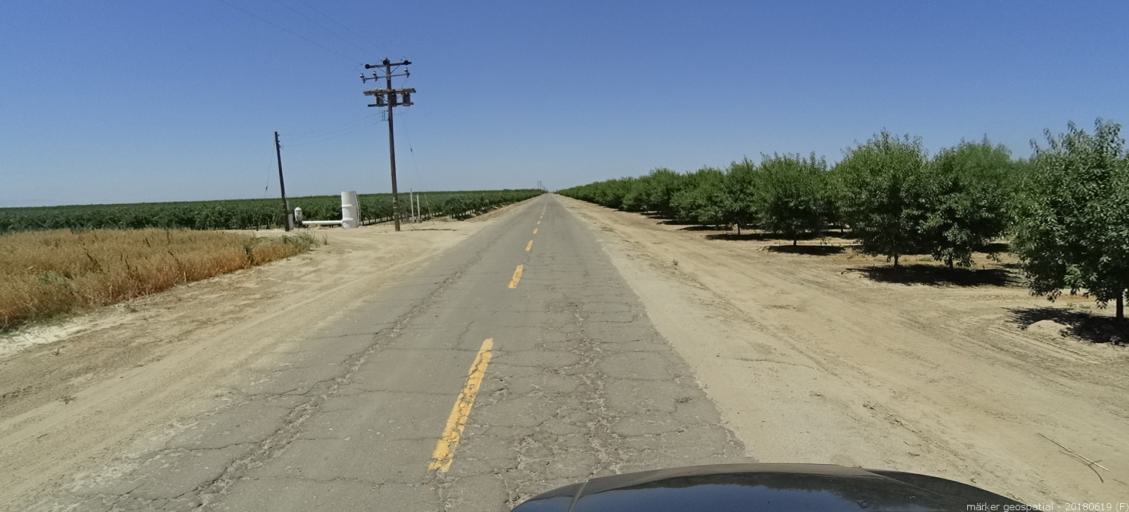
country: US
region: California
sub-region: Madera County
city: Parkwood
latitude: 36.8658
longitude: -120.1410
